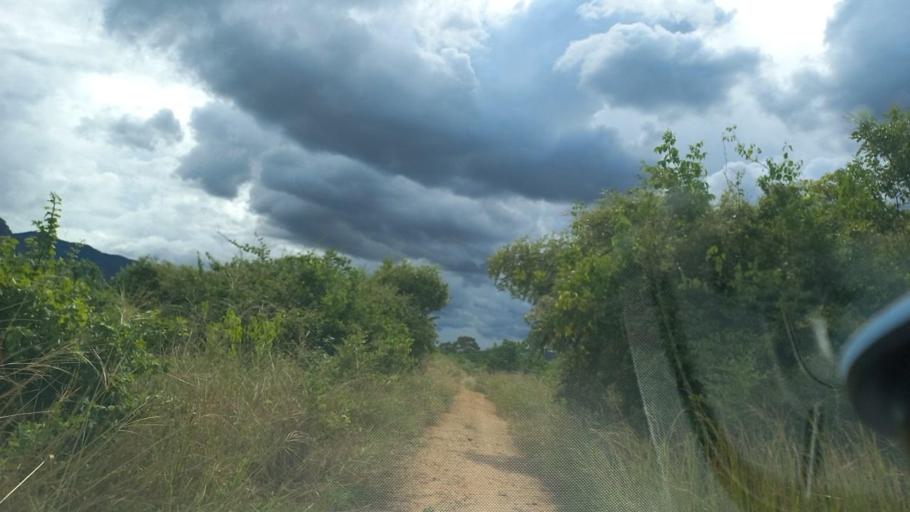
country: ZM
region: Lusaka
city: Luangwa
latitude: -15.6517
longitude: 30.3444
